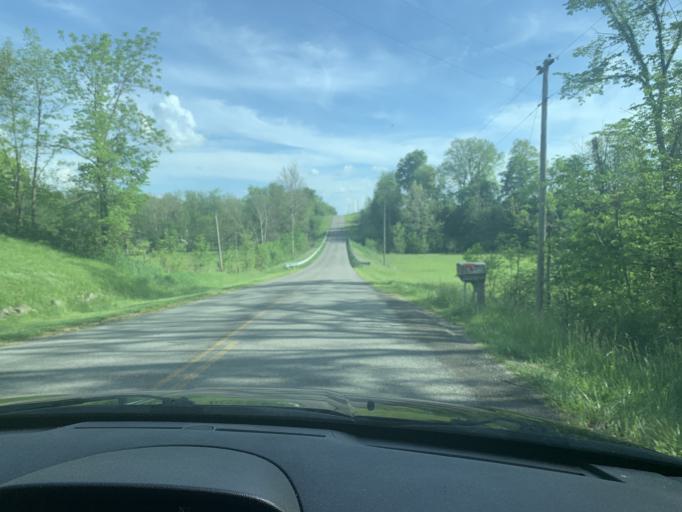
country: US
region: Ohio
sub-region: Logan County
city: De Graff
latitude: 40.3062
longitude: -84.0115
